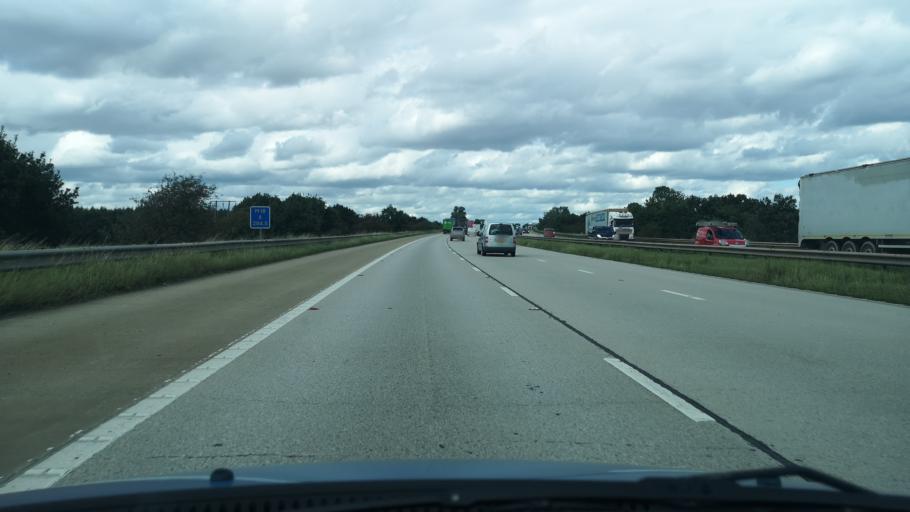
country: GB
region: England
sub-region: Doncaster
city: Hatfield
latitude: 53.6057
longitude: -0.9907
